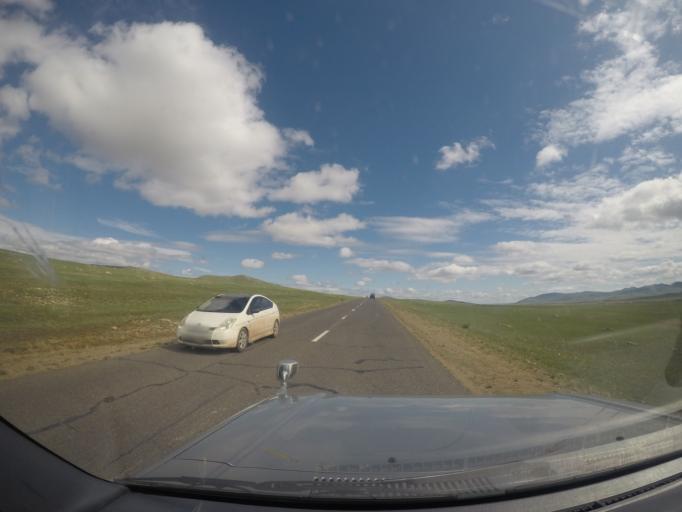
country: MN
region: Hentiy
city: Modot
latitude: 47.6272
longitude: 109.1712
